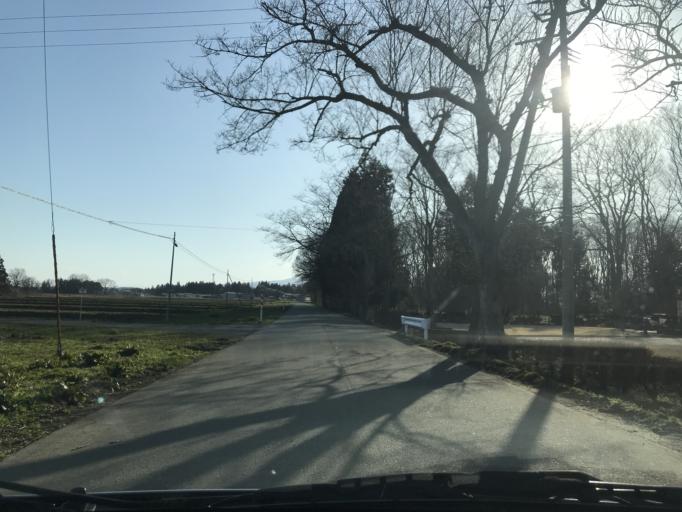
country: JP
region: Iwate
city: Kitakami
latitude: 39.2589
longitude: 141.0415
